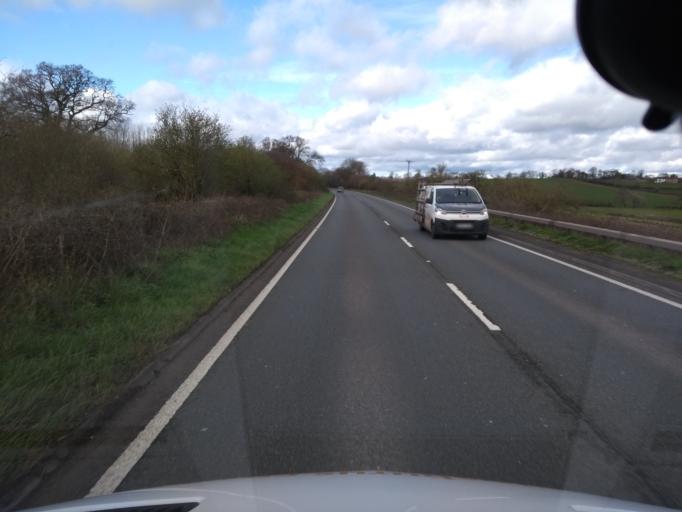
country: GB
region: England
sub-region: Somerset
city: Stoke-sub-Hamdon
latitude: 50.9511
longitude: -2.6996
